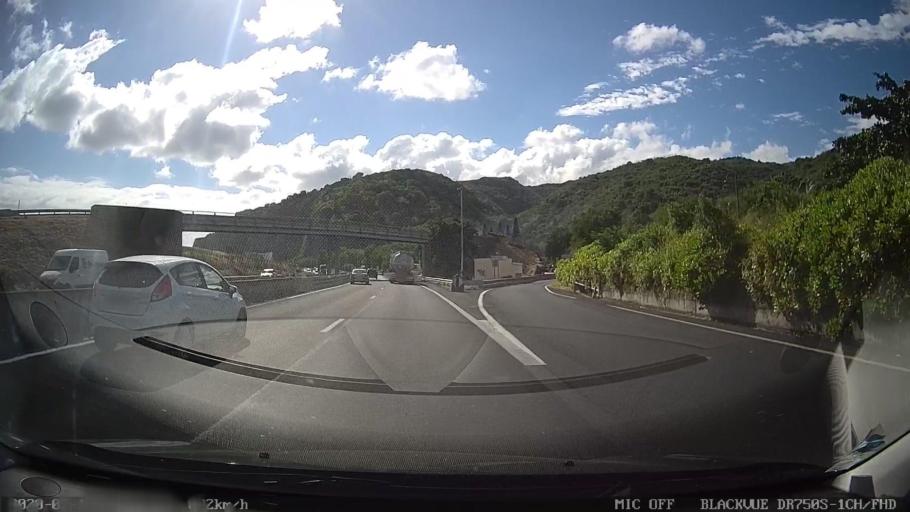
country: RE
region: Reunion
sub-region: Reunion
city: La Possession
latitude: -20.9243
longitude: 55.3431
